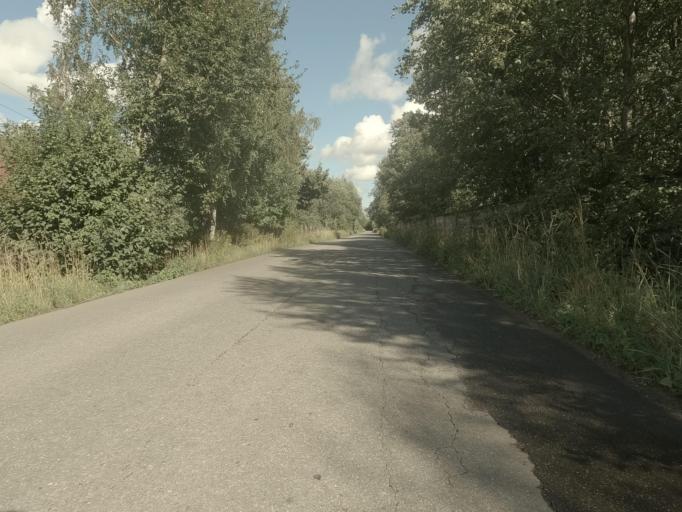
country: RU
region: Leningrad
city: Yanino Vtoroye
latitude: 59.9837
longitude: 30.5902
